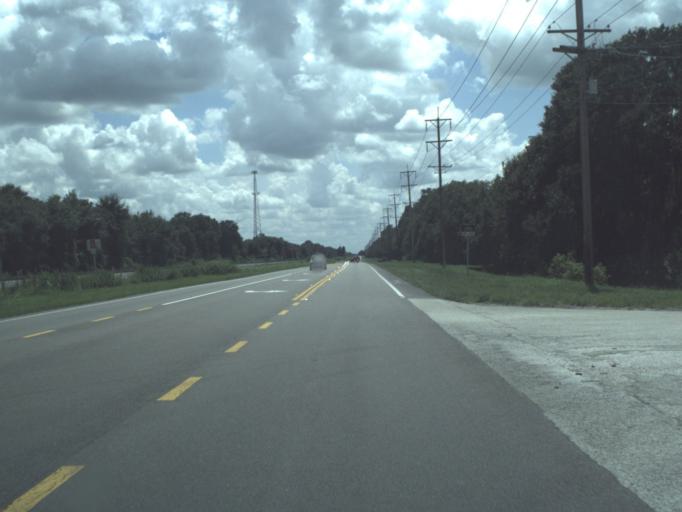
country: US
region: Florida
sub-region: Pasco County
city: Crystal Springs
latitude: 28.1094
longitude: -82.1442
